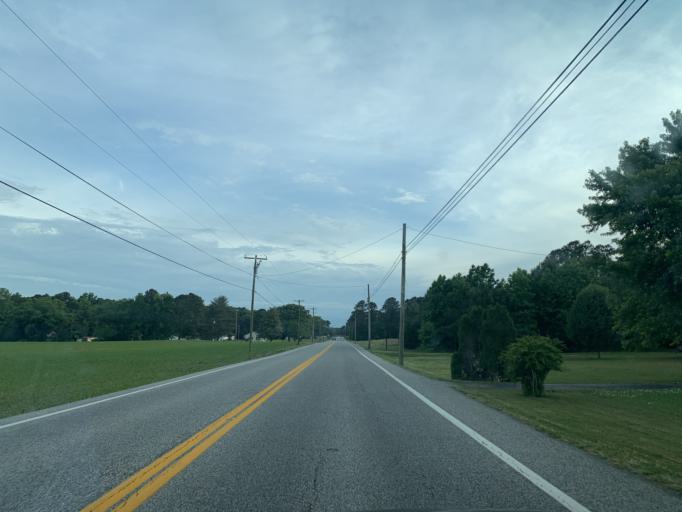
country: US
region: Maryland
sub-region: Worcester County
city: Snow Hill
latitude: 38.1519
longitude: -75.4082
